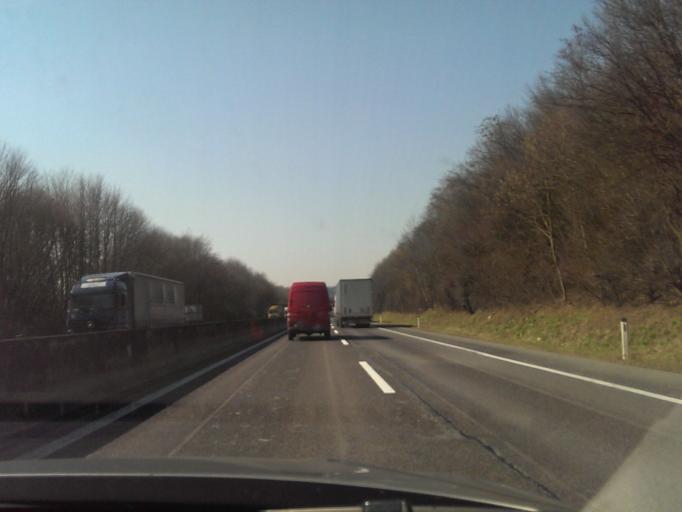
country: AT
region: Upper Austria
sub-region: Politischer Bezirk Ried im Innkreis
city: Ried im Innkreis
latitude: 48.2423
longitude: 13.5430
